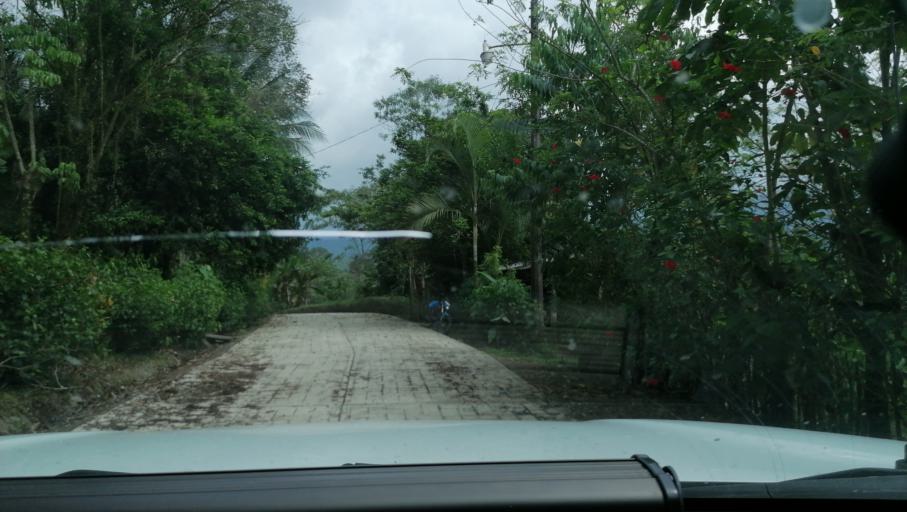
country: MX
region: Chiapas
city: Ocotepec
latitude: 17.3273
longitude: -93.1731
